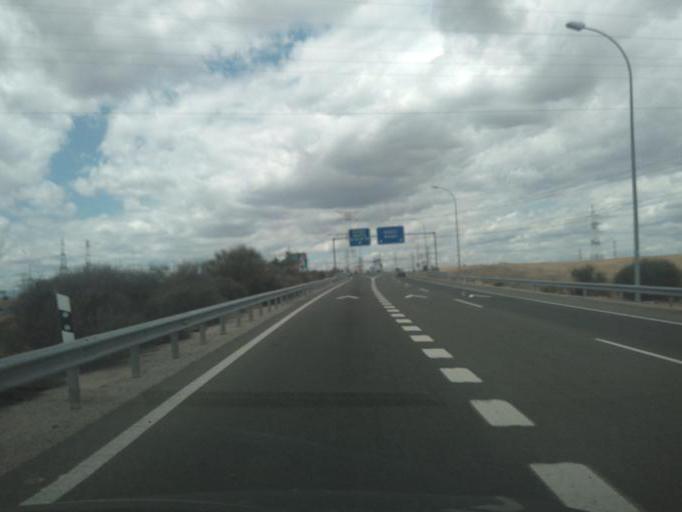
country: ES
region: Madrid
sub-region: Provincia de Madrid
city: San Sebastian de los Reyes
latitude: 40.5593
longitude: -3.5905
